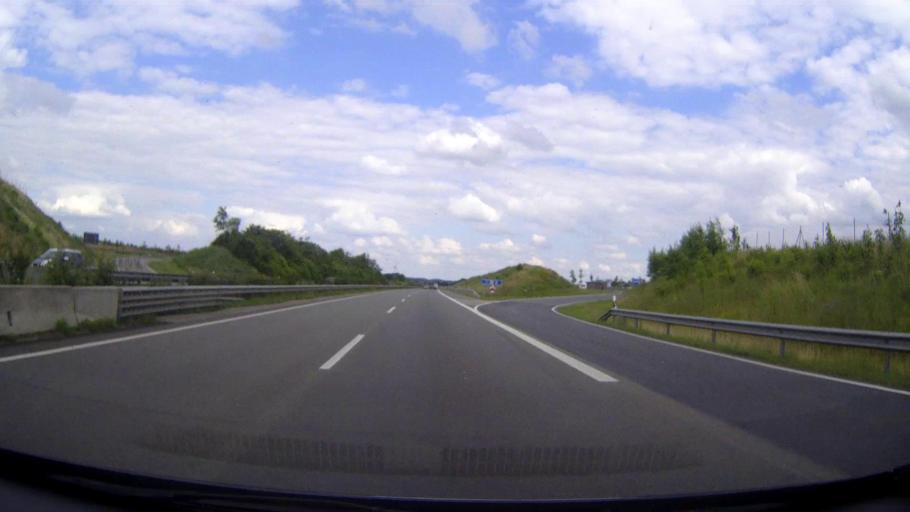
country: DE
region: Schleswig-Holstein
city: Weede
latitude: 53.9184
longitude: 10.3833
